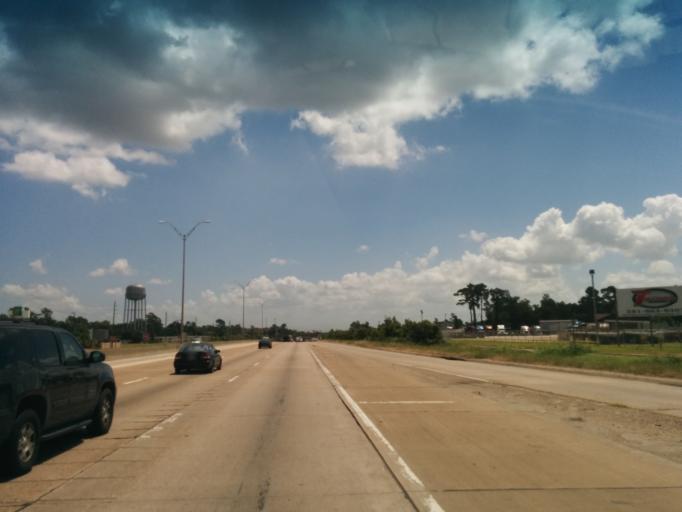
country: US
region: Texas
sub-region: Harris County
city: Channelview
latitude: 29.7832
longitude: -95.1110
